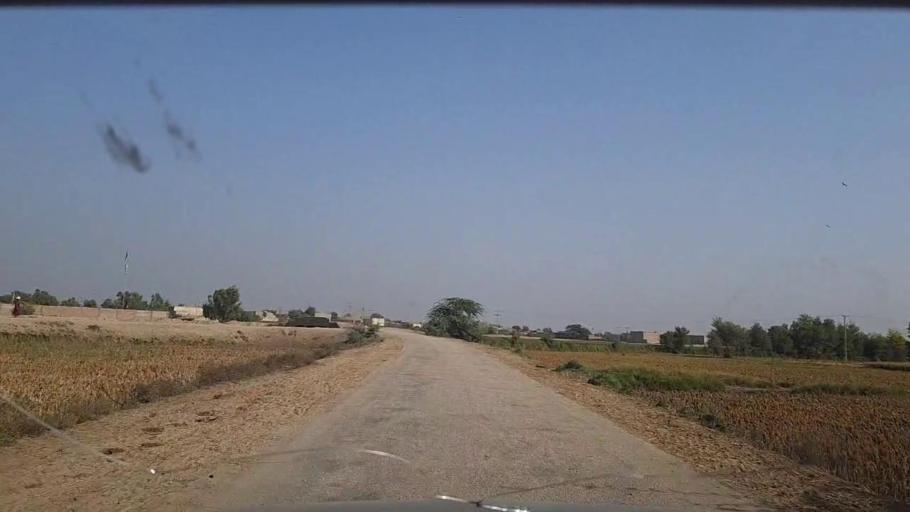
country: PK
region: Sindh
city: Shikarpur
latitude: 28.1163
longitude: 68.5766
